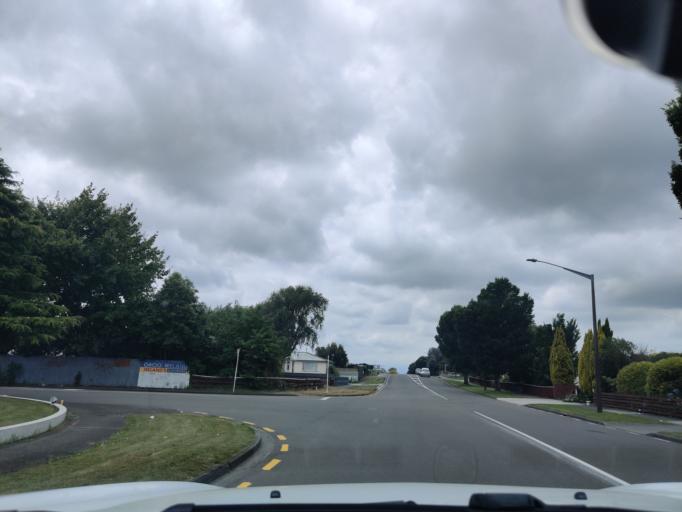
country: NZ
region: Manawatu-Wanganui
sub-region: Palmerston North City
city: Palmerston North
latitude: -40.3493
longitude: 175.5885
